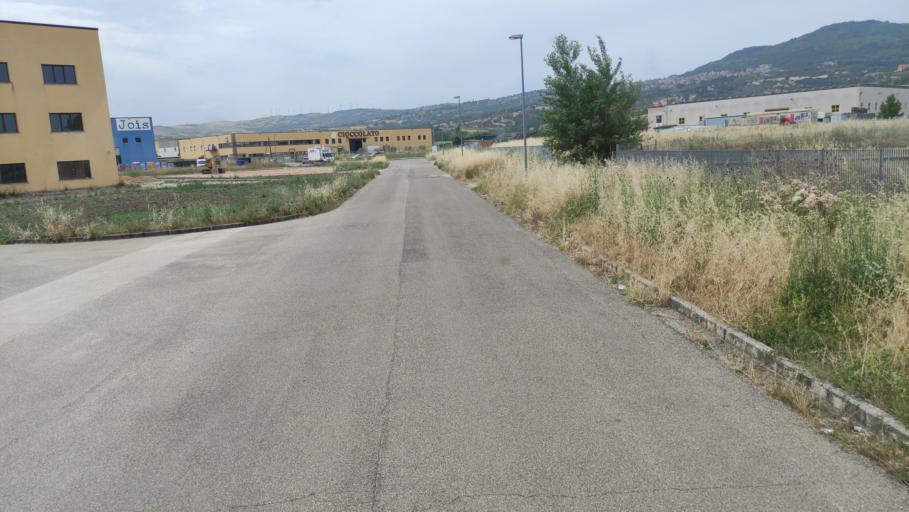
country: IT
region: Campania
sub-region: Provincia di Avellino
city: Sturno
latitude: 41.0503
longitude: 15.1218
